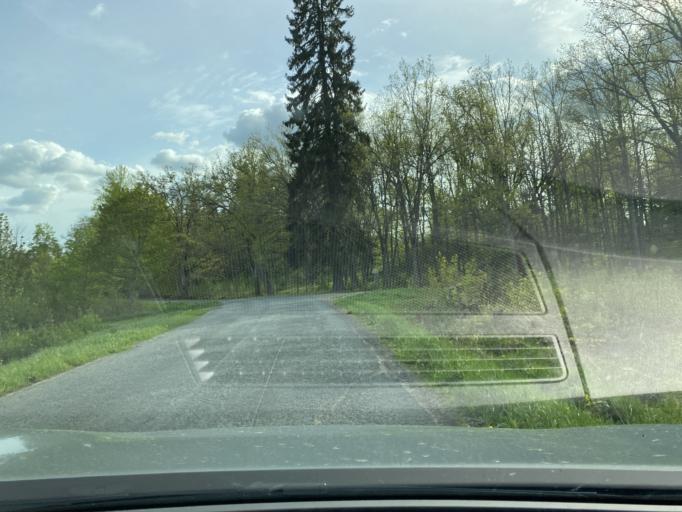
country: FI
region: Varsinais-Suomi
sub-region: Salo
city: Kiikala
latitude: 60.4467
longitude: 23.5540
